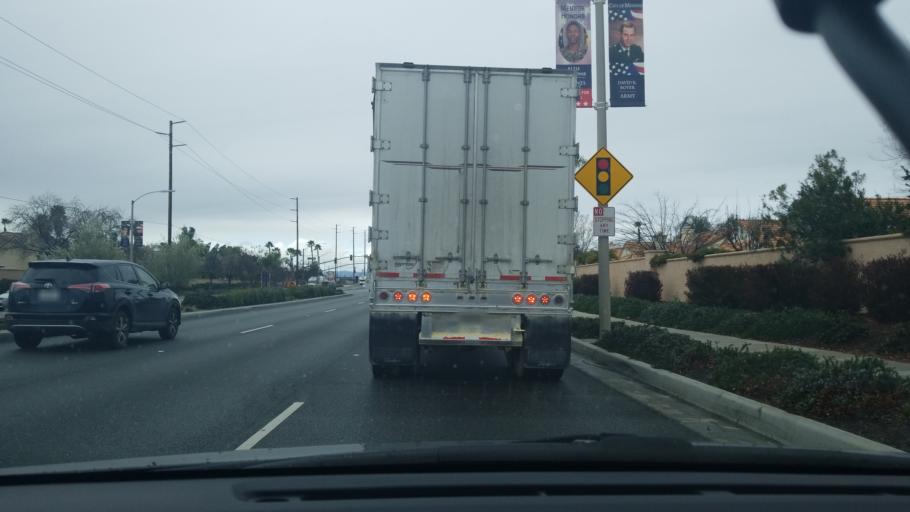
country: US
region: California
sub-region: Riverside County
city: Sun City
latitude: 33.6852
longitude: -117.1652
